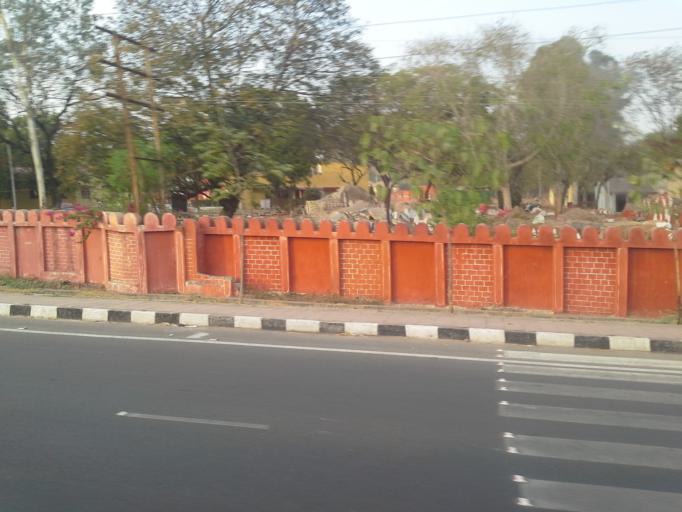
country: IN
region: Telangana
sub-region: Hyderabad
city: Hyderabad
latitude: 17.3748
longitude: 78.3985
